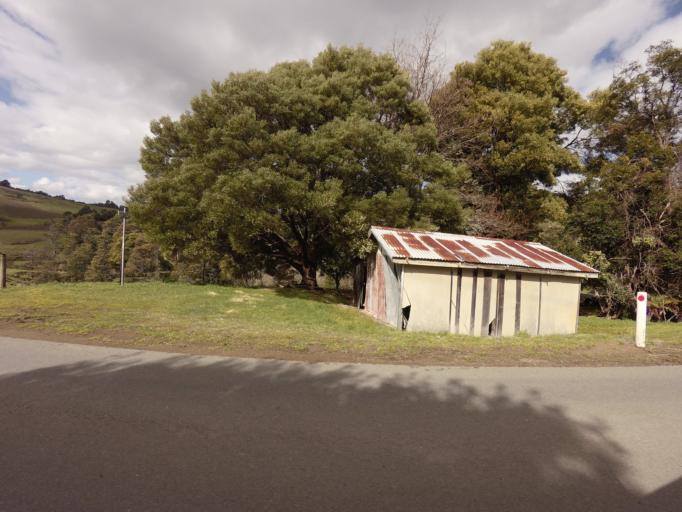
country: AU
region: Tasmania
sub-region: Huon Valley
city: Geeveston
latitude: -43.2431
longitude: 146.9914
